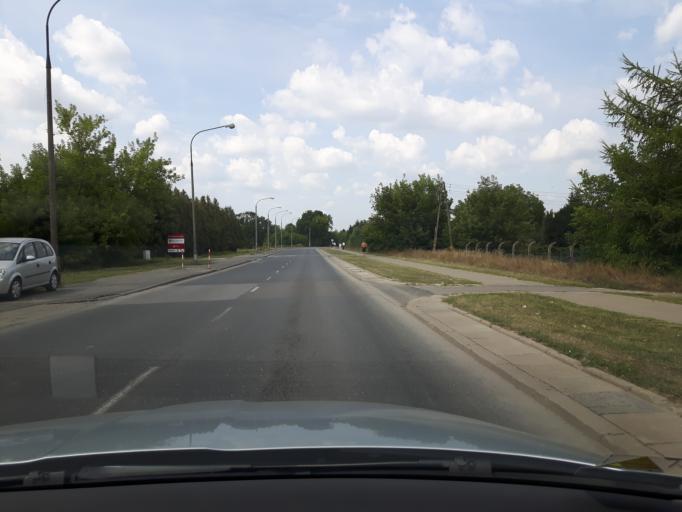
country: PL
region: Masovian Voivodeship
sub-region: Warszawa
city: Wilanow
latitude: 52.1905
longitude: 21.0790
